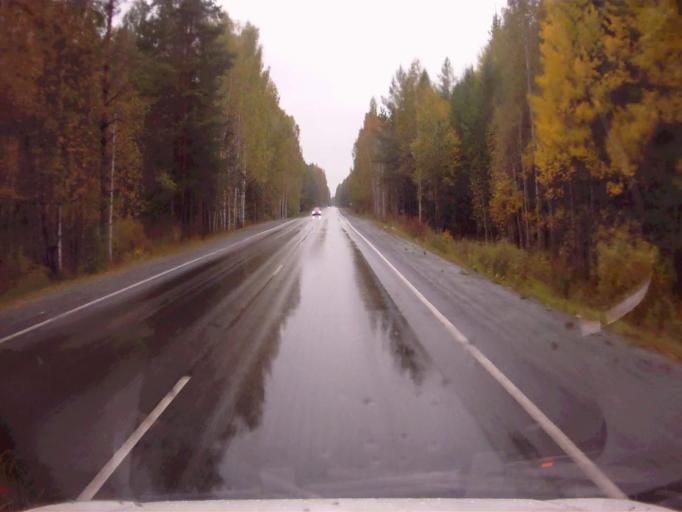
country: RU
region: Chelyabinsk
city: Tayginka
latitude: 55.5808
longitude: 60.6407
